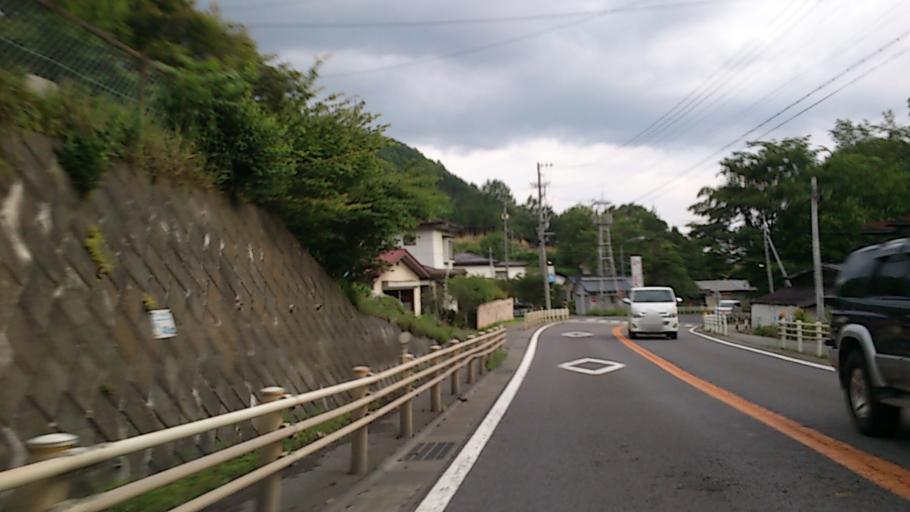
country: JP
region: Nagano
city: Suwa
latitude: 36.1226
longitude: 138.1021
